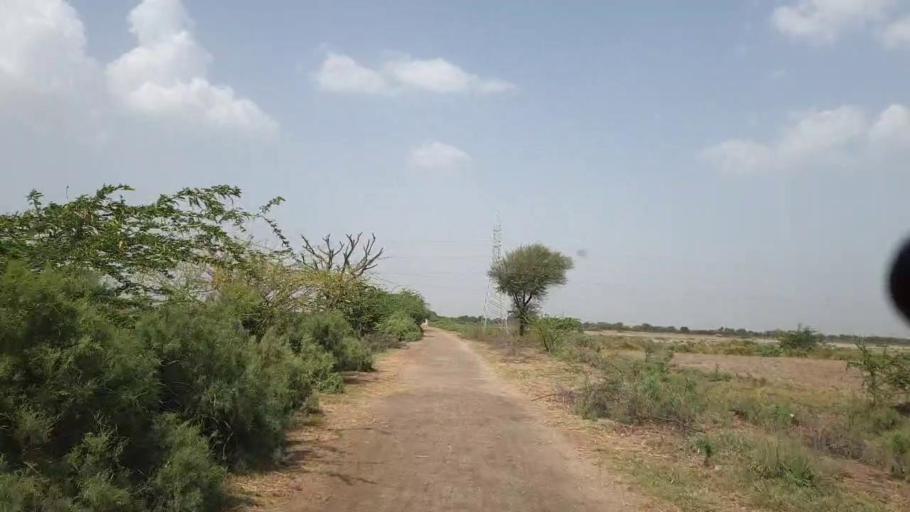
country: PK
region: Sindh
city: Tando Ghulam Ali
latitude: 25.0696
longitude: 68.8110
